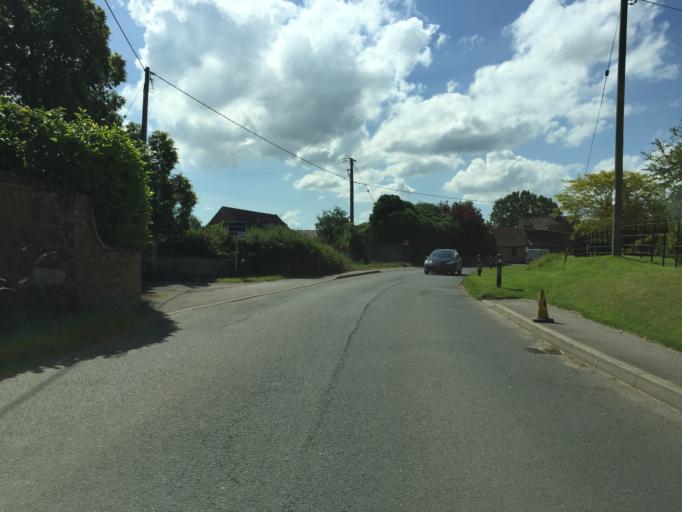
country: GB
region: England
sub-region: Gloucestershire
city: Dursley
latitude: 51.7296
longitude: -2.3771
